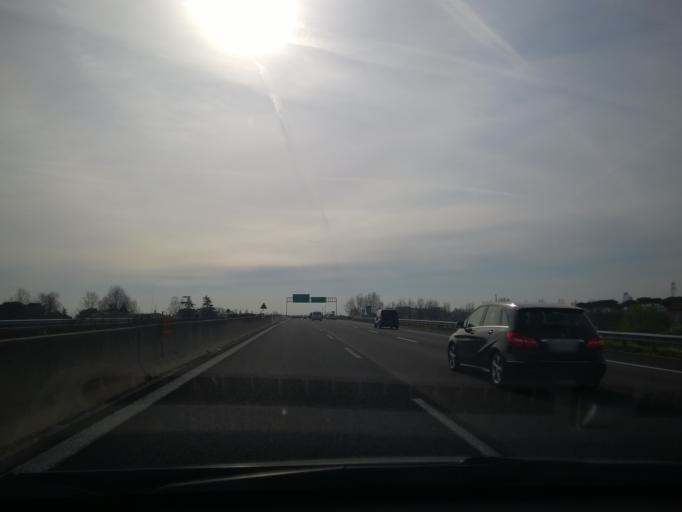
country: IT
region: Emilia-Romagna
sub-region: Forli-Cesena
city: Santa Maria Nuova
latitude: 44.1991
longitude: 12.2154
